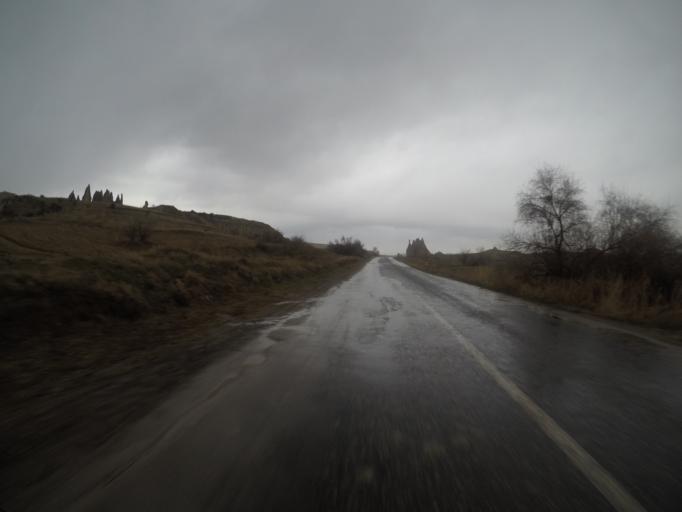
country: TR
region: Nevsehir
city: Goereme
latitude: 38.6622
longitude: 34.8319
